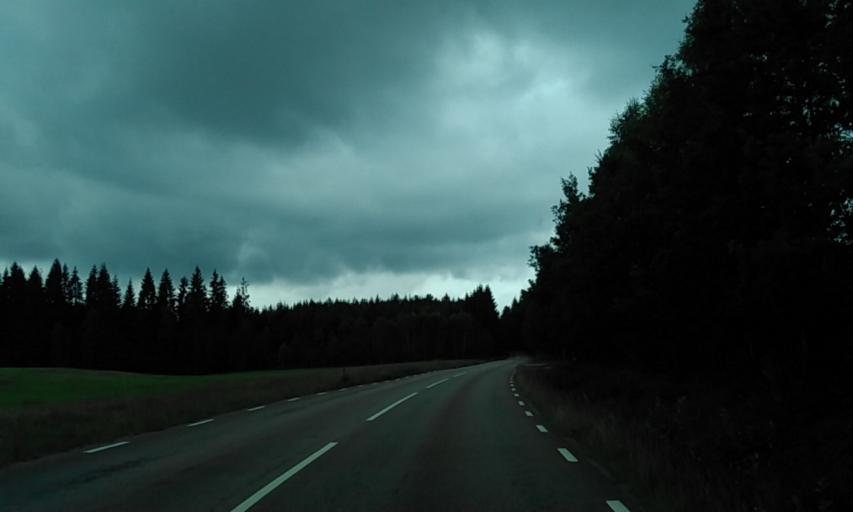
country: SE
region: Vaestra Goetaland
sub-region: Bollebygds Kommun
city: Bollebygd
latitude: 57.7147
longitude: 12.5848
